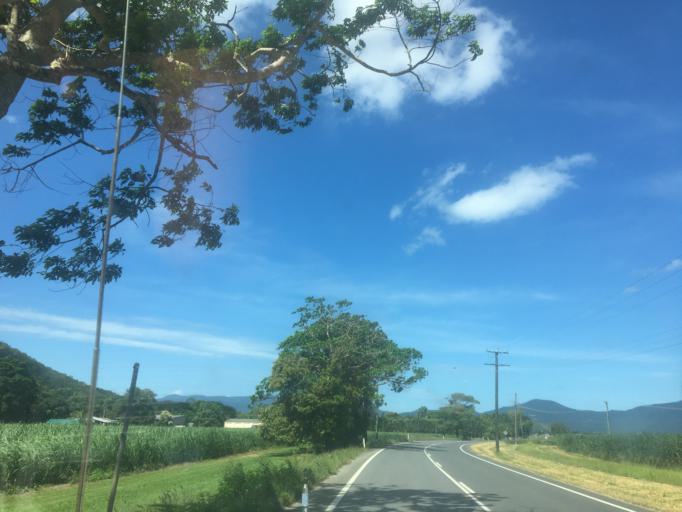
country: AU
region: Queensland
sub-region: Cairns
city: Woree
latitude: -17.0642
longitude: 145.7558
